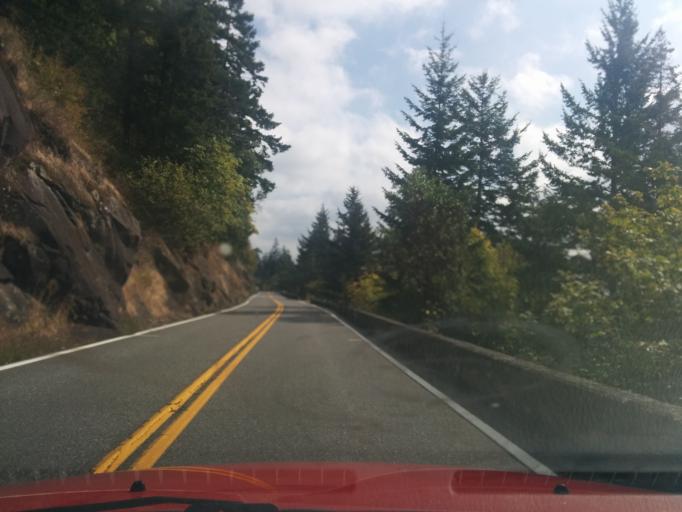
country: US
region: Washington
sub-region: Whatcom County
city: Bellingham
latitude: 48.6369
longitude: -122.4759
